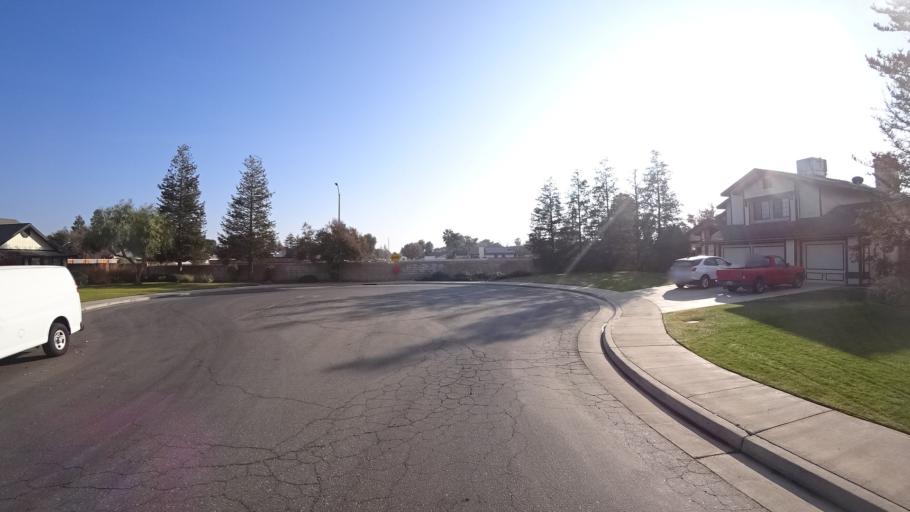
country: US
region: California
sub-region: Kern County
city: Rosedale
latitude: 35.3506
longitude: -119.1597
